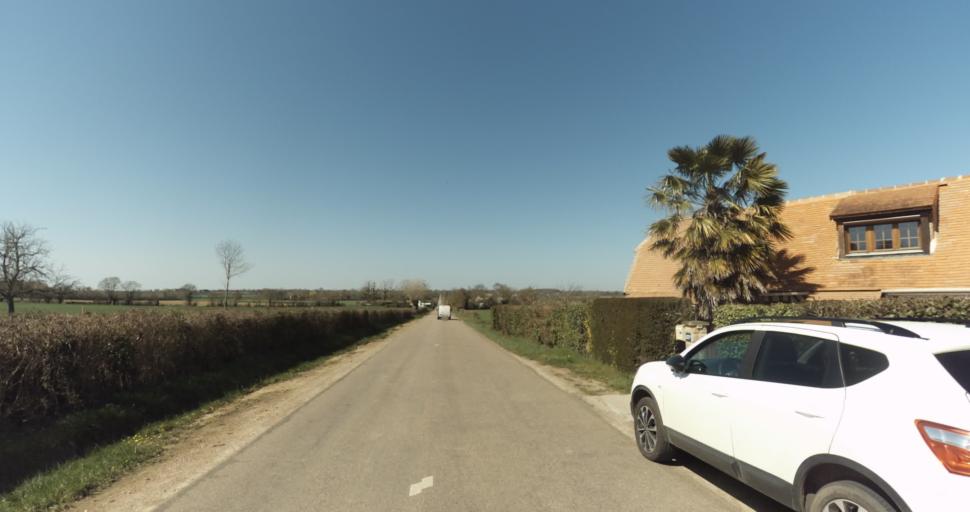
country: FR
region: Lower Normandy
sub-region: Departement du Calvados
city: Saint-Pierre-sur-Dives
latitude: 48.9917
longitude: 0.0226
